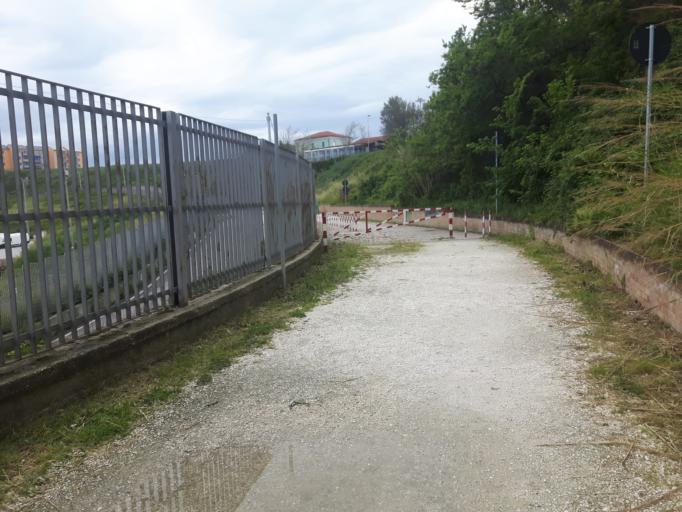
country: IT
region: Abruzzo
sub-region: Provincia di Chieti
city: Vasto
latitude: 42.1720
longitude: 14.7097
